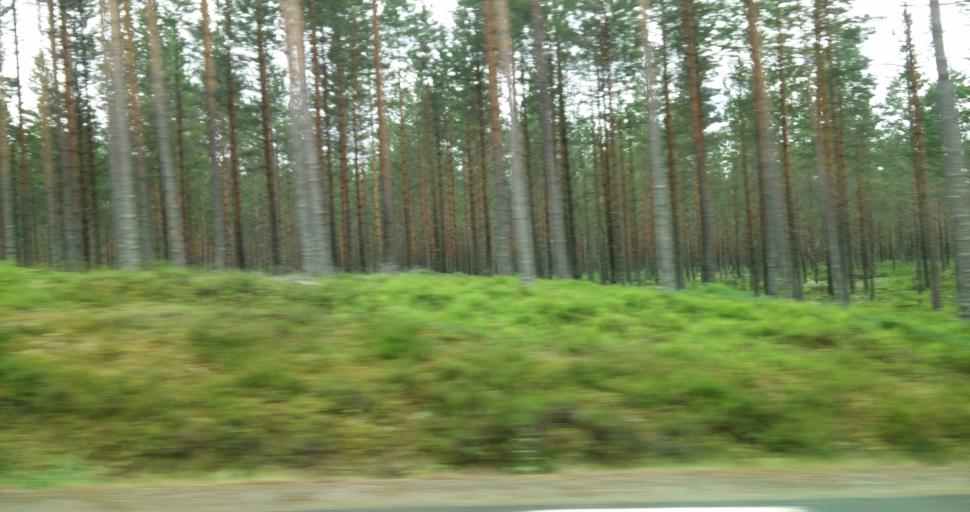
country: SE
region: Vaermland
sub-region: Munkfors Kommun
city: Munkfors
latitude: 59.9691
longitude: 13.5137
